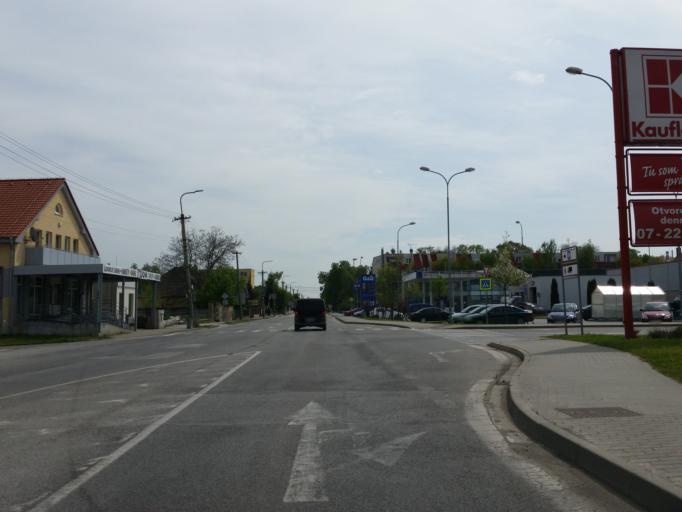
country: SK
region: Trnavsky
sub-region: Okres Galanta
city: Galanta
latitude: 48.2815
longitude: 17.7361
